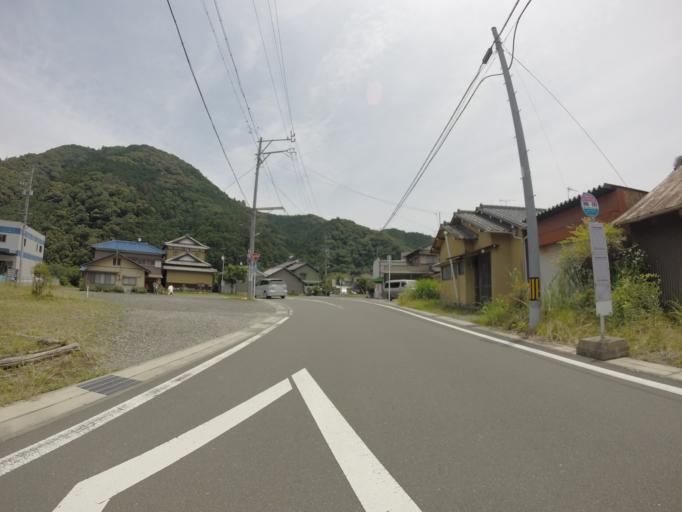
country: JP
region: Shizuoka
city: Shizuoka-shi
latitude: 35.0060
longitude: 138.2826
